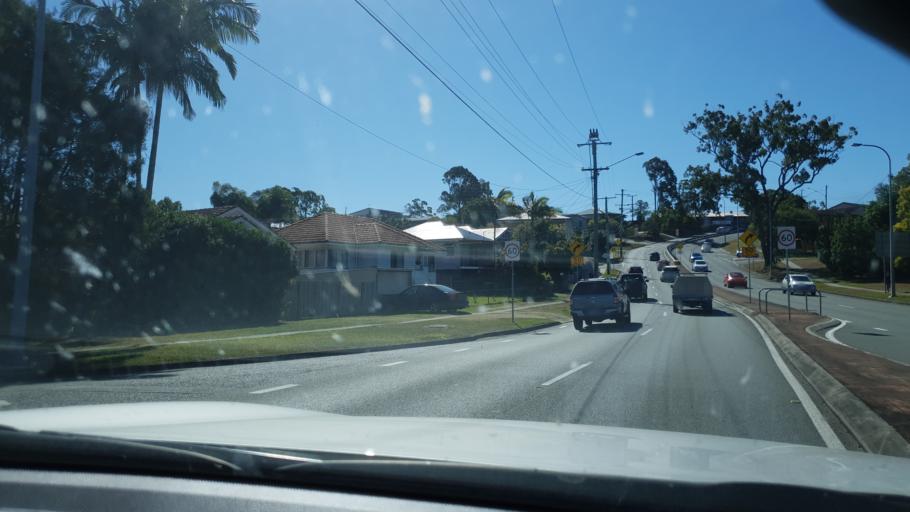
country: AU
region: Queensland
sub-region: Brisbane
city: Everton Park
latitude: -27.4006
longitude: 152.9865
